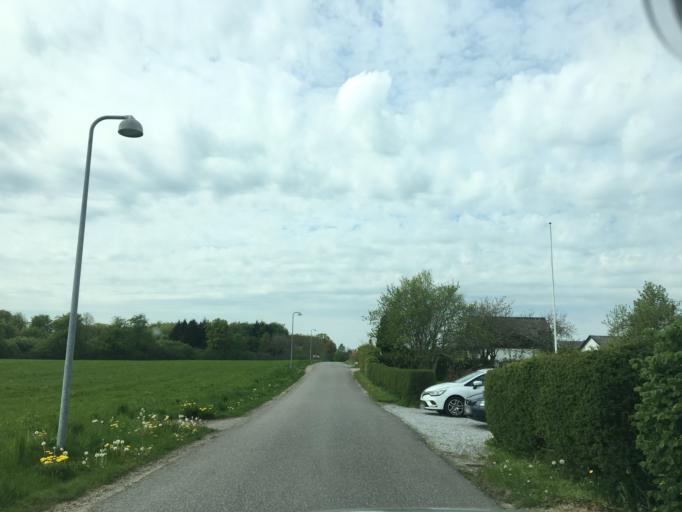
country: DK
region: Zealand
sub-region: Lejre Kommune
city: Osted
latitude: 55.5542
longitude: 11.9475
